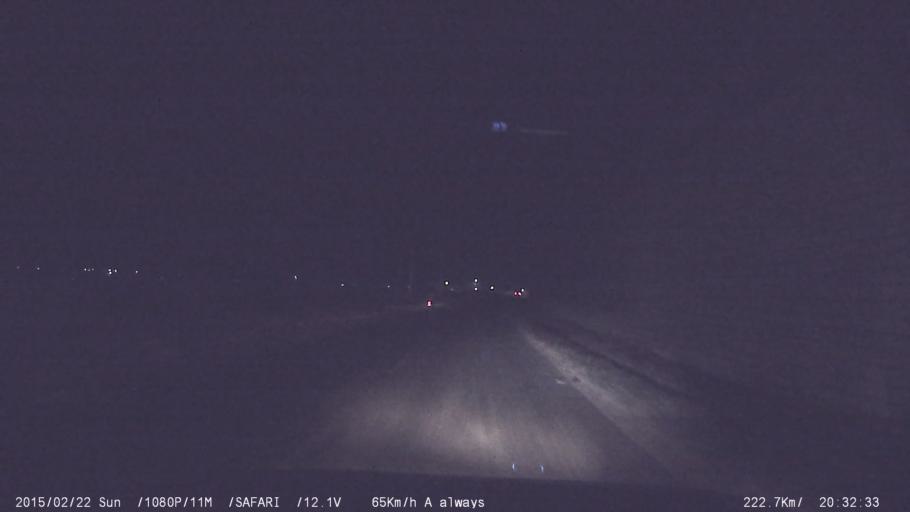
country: IN
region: Tamil Nadu
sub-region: Dindigul
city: Dindigul
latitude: 10.3489
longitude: 77.9498
